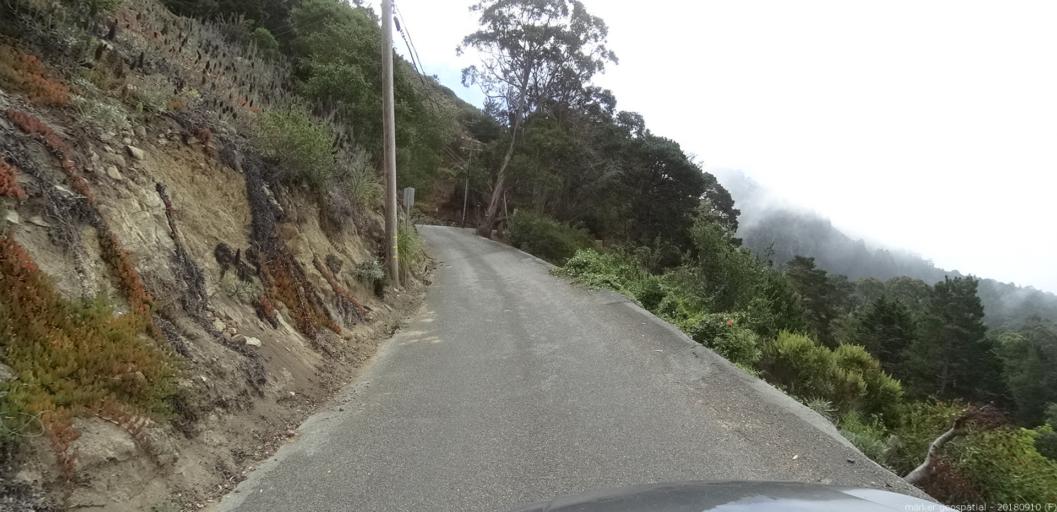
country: US
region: California
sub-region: Monterey County
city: Carmel-by-the-Sea
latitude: 36.4998
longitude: -121.9318
